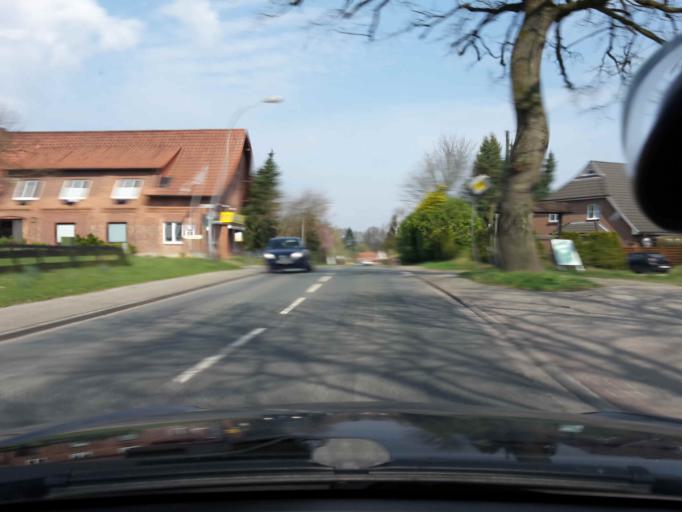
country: DE
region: Lower Saxony
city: Harmstorf
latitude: 53.3666
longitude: 9.9825
